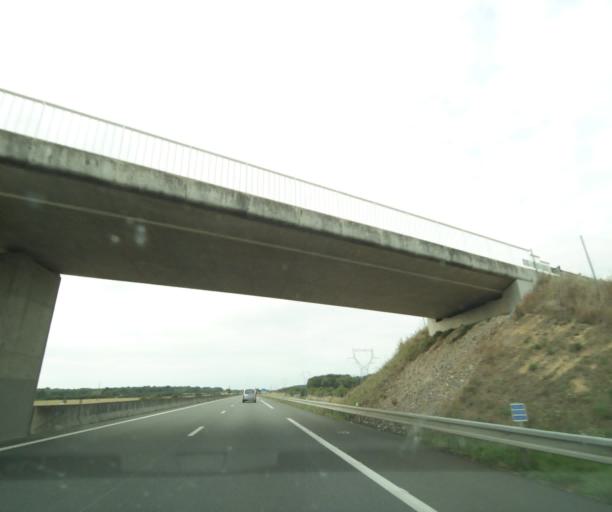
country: FR
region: Centre
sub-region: Departement d'Indre-et-Loire
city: Saint-Antoine-du-Rocher
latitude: 47.5108
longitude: 0.6348
